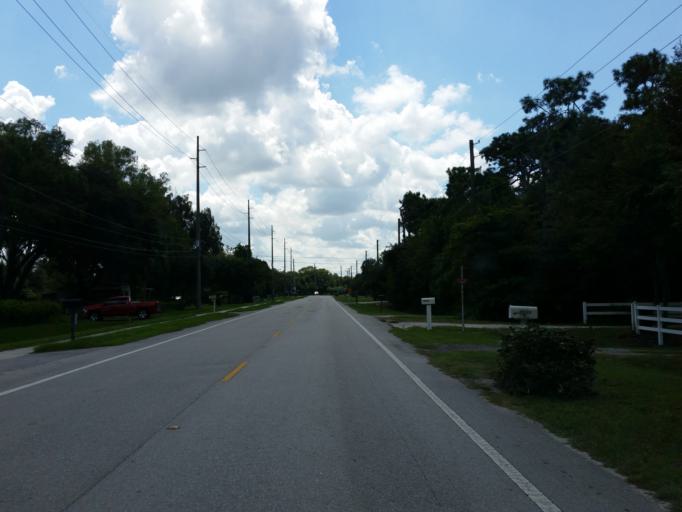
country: US
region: Florida
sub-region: Hillsborough County
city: Riverview
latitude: 27.8344
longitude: -82.3019
